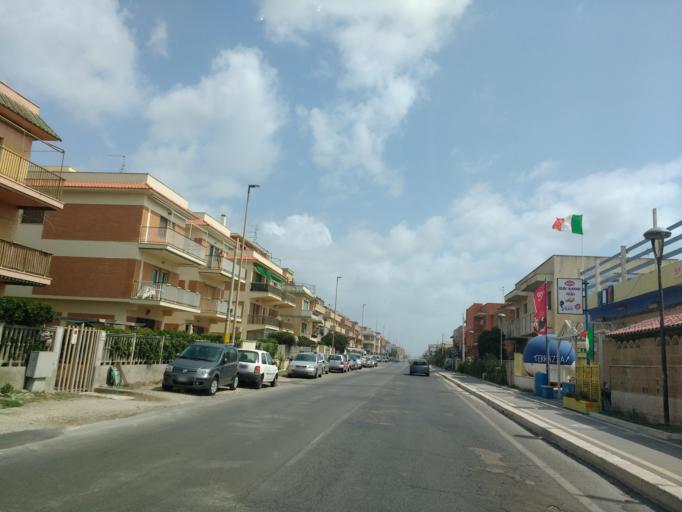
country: IT
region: Latium
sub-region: Citta metropolitana di Roma Capitale
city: Ardea
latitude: 41.5919
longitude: 12.4934
